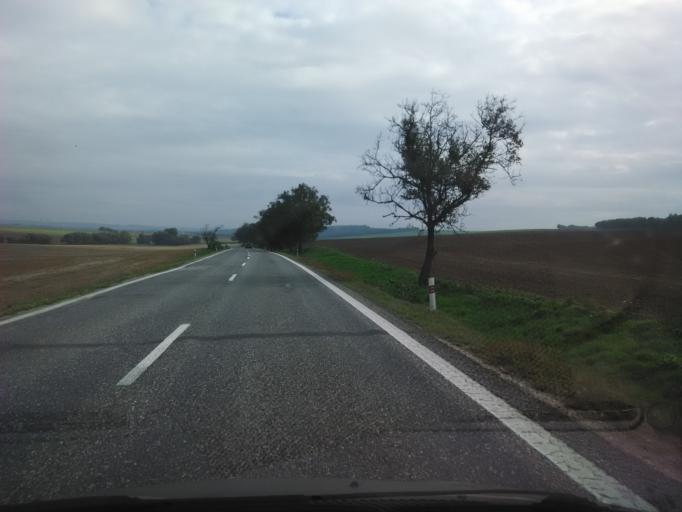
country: SK
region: Nitriansky
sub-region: Okres Nitra
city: Vrable
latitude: 48.2789
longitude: 18.2215
